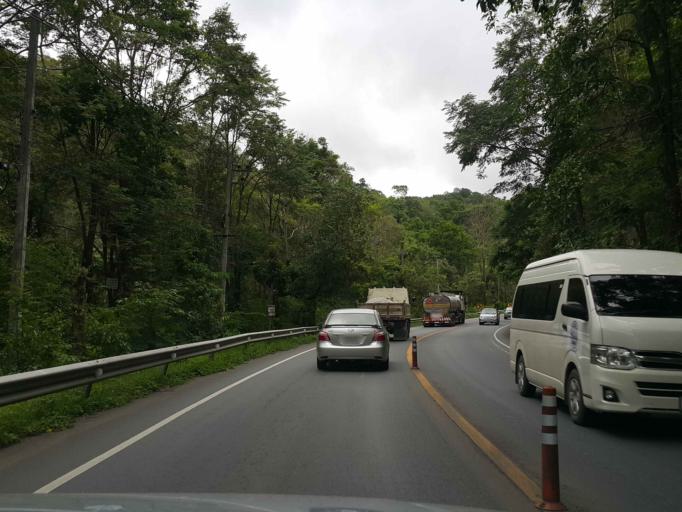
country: TH
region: Tak
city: Tak
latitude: 16.8030
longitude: 98.9563
